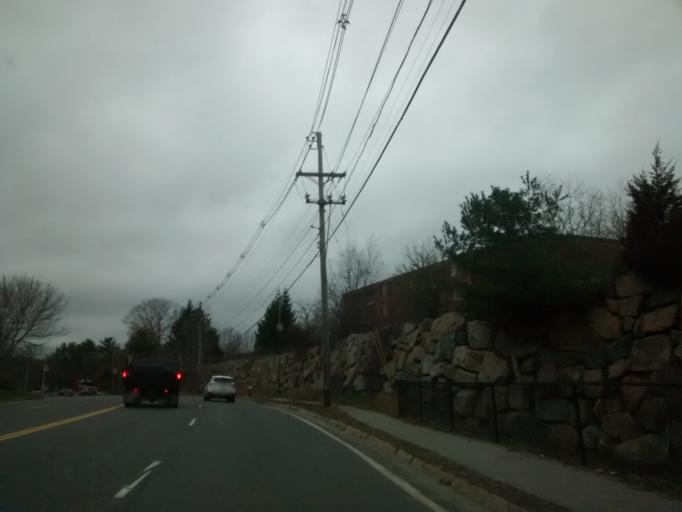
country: US
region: Massachusetts
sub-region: Worcester County
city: Milford
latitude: 42.1621
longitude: -71.5061
